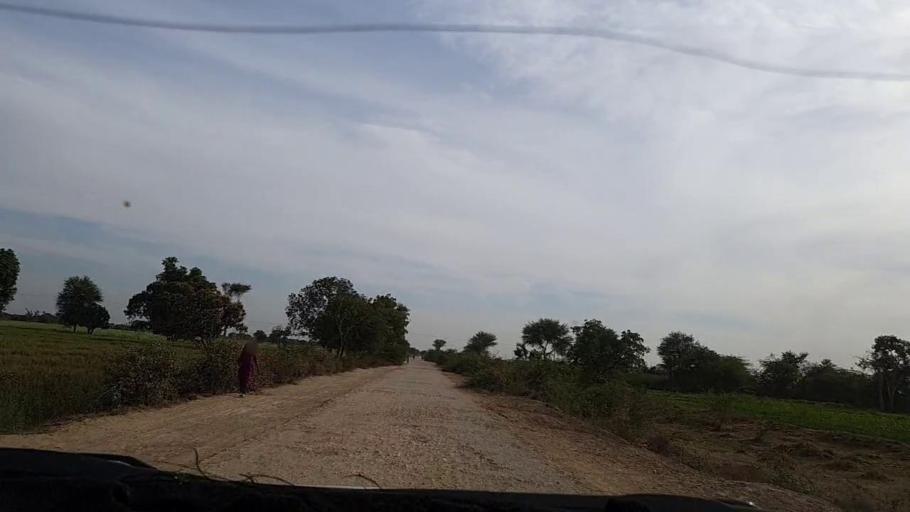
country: PK
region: Sindh
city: Dhoro Naro
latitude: 25.4295
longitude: 69.5218
